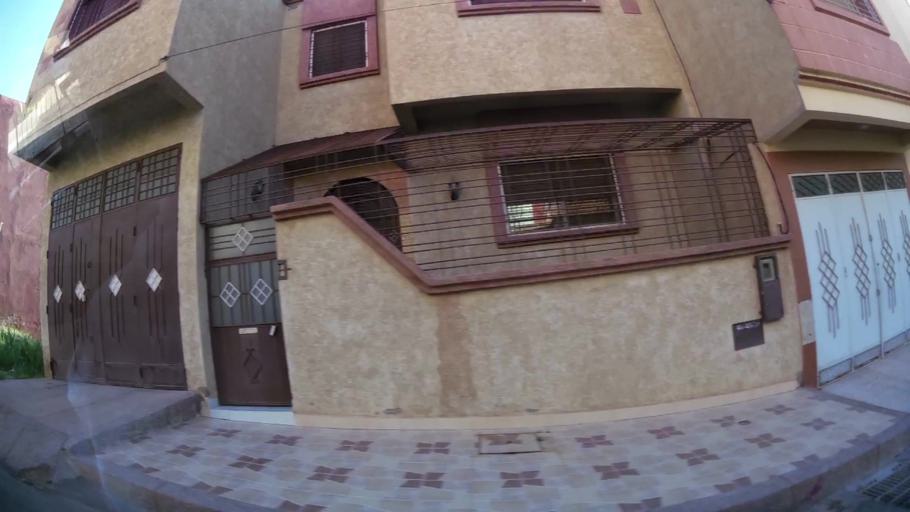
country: MA
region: Oriental
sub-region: Oujda-Angad
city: Oujda
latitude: 34.6762
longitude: -1.9392
